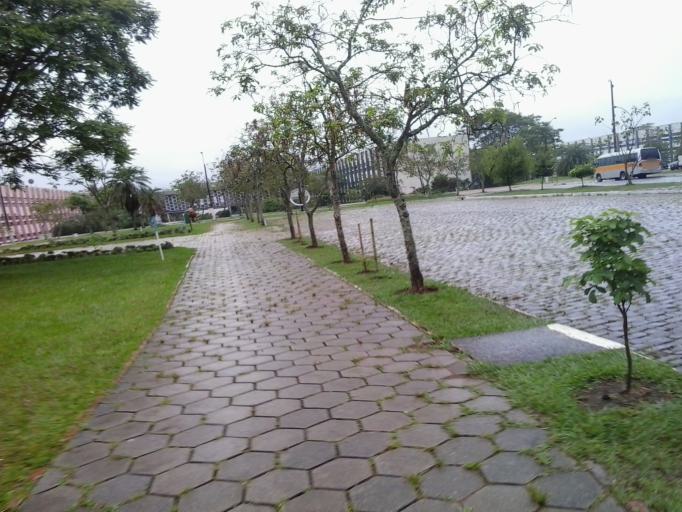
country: BR
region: Rio Grande do Sul
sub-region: Santa Maria
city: Santa Maria
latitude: -29.7202
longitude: -53.7170
